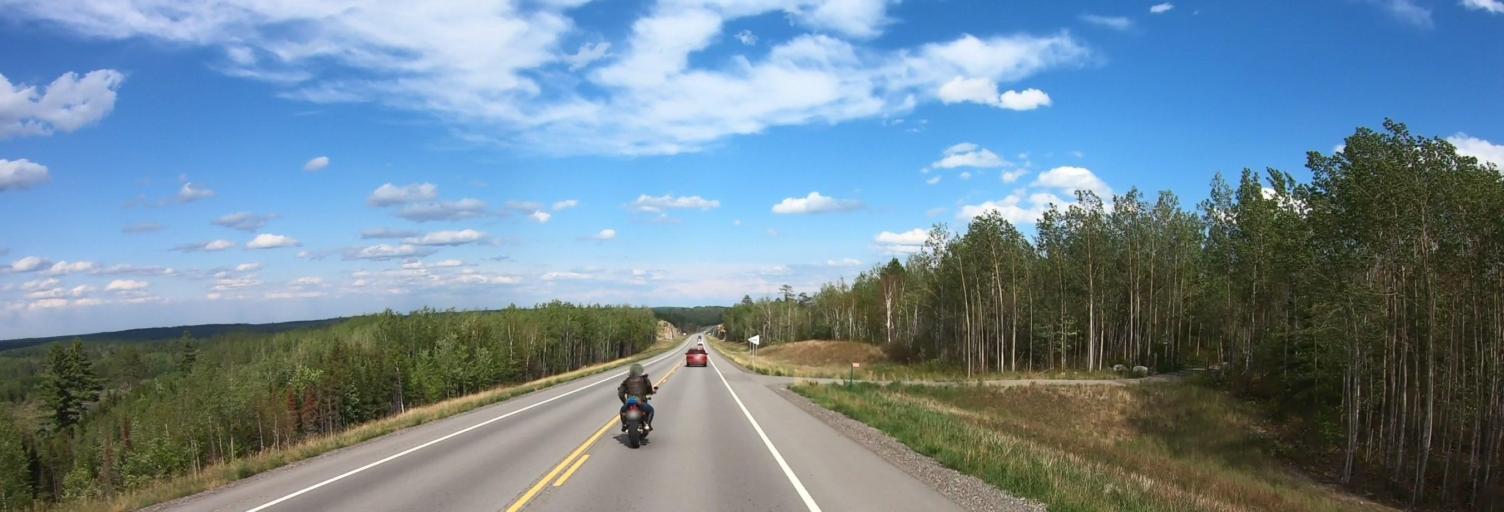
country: US
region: Minnesota
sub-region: Saint Louis County
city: Babbitt
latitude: 47.8441
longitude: -92.1371
